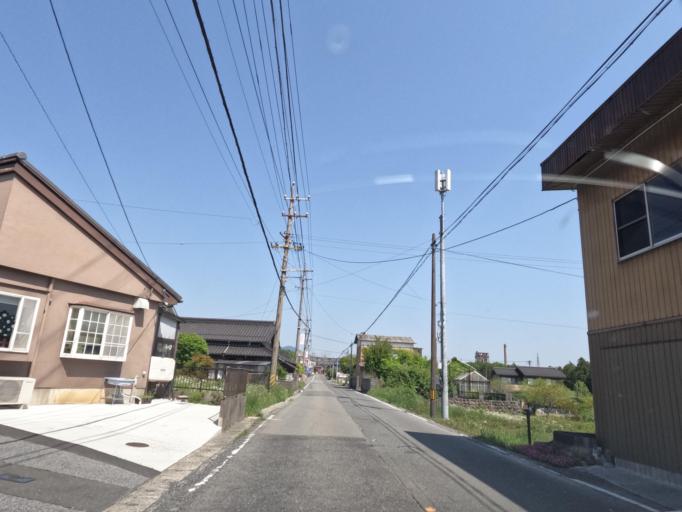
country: JP
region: Mie
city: Komono
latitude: 35.1455
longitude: 136.5009
